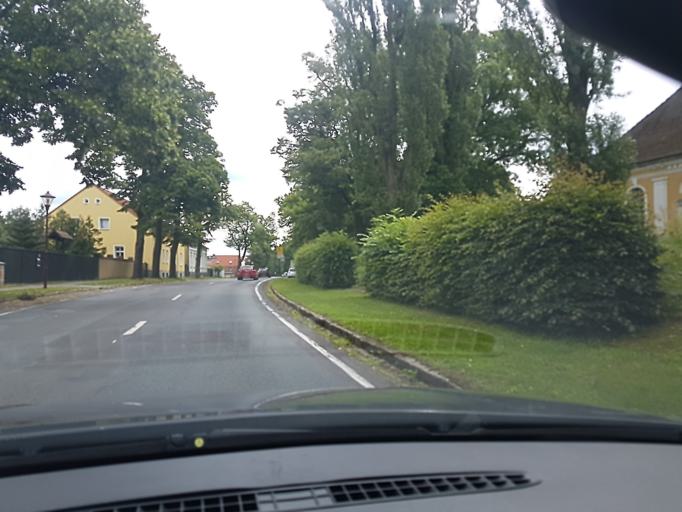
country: DE
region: Brandenburg
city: Velten
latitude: 52.6770
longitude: 13.1426
